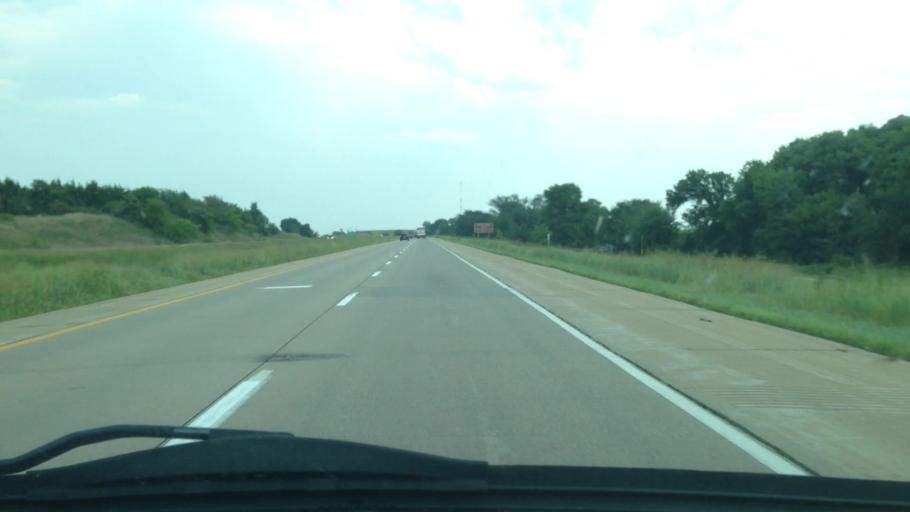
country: US
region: Iowa
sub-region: Buchanan County
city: Jesup
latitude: 42.3611
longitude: -92.0822
